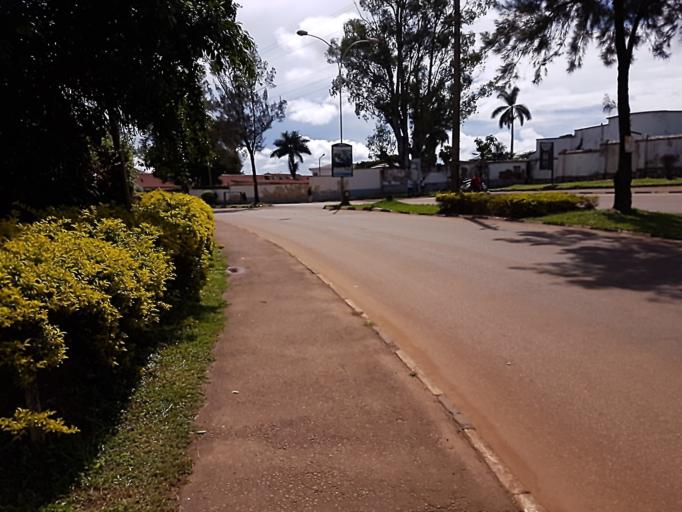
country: UG
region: Central Region
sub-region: Wakiso District
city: Entebbe
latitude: 0.0564
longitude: 32.4678
